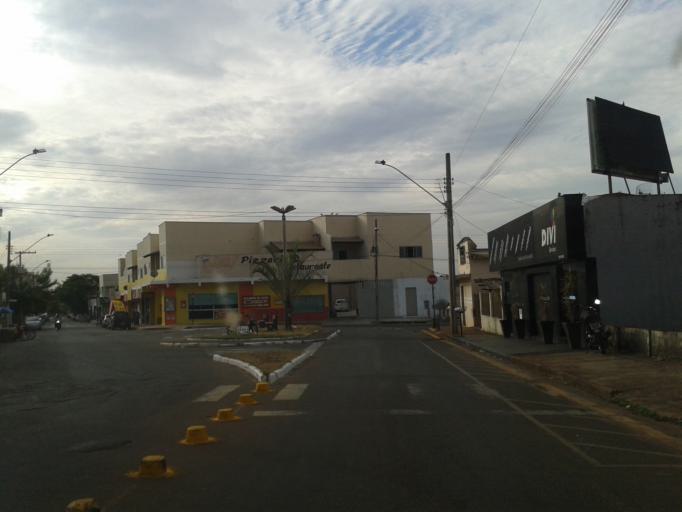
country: BR
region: Minas Gerais
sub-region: Ituiutaba
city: Ituiutaba
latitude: -18.9839
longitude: -49.4509
